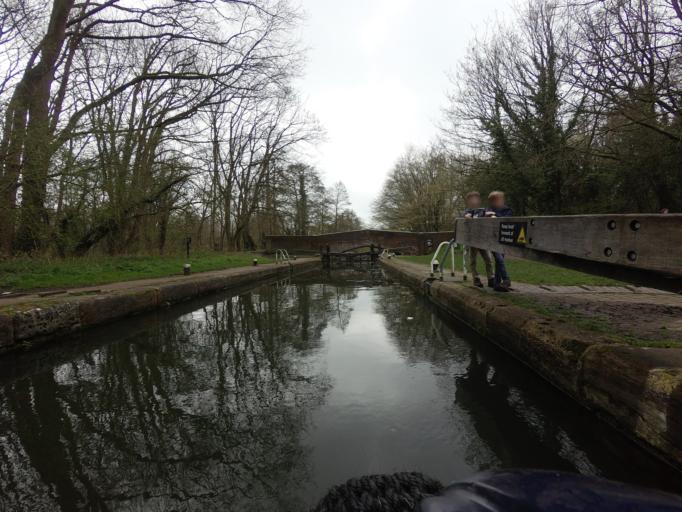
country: GB
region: England
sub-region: Hertfordshire
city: Watford
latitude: 51.6645
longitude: -0.4269
